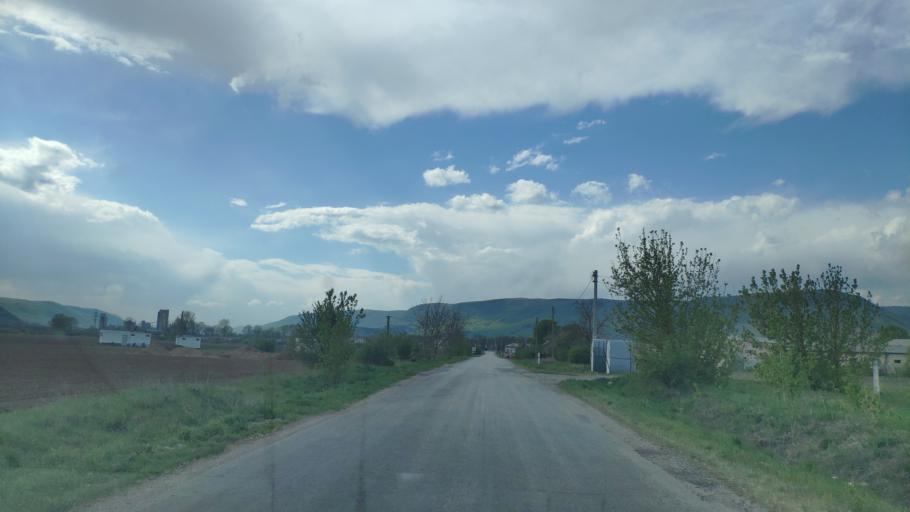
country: SK
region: Kosicky
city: Medzev
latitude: 48.5952
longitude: 20.8882
